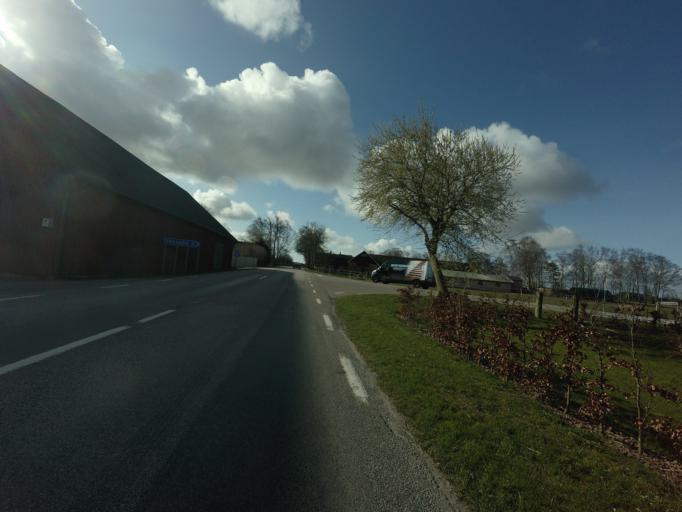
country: SE
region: Skane
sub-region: Helsingborg
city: Odakra
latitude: 56.1603
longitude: 12.6784
